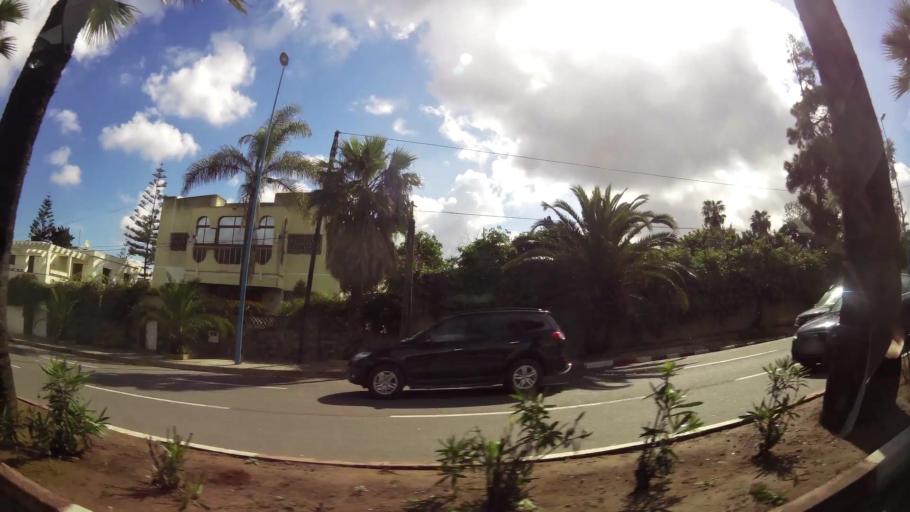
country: MA
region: Grand Casablanca
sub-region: Casablanca
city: Casablanca
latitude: 33.5510
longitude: -7.6230
